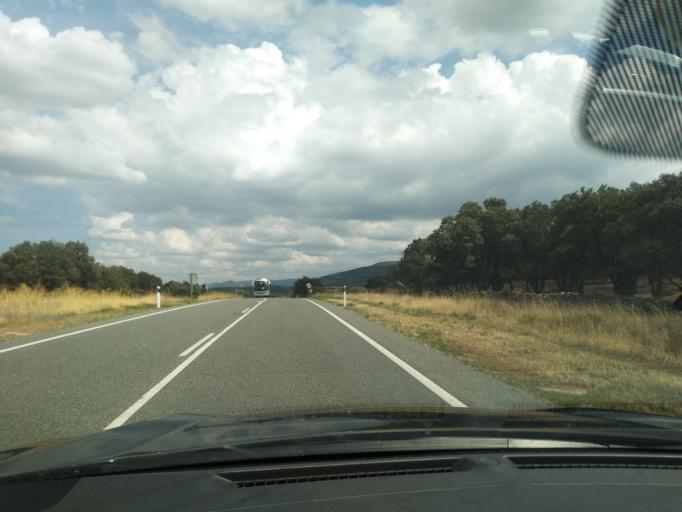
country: ES
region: Castille and Leon
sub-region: Provincia de Segovia
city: Ortigosa del Monte
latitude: 40.8544
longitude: -4.1194
